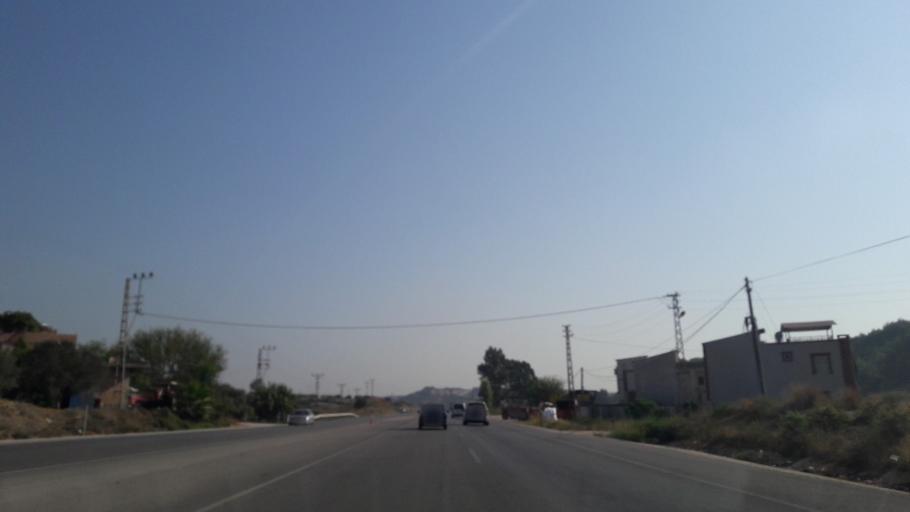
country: TR
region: Adana
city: Yuregir
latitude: 37.0665
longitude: 35.4501
